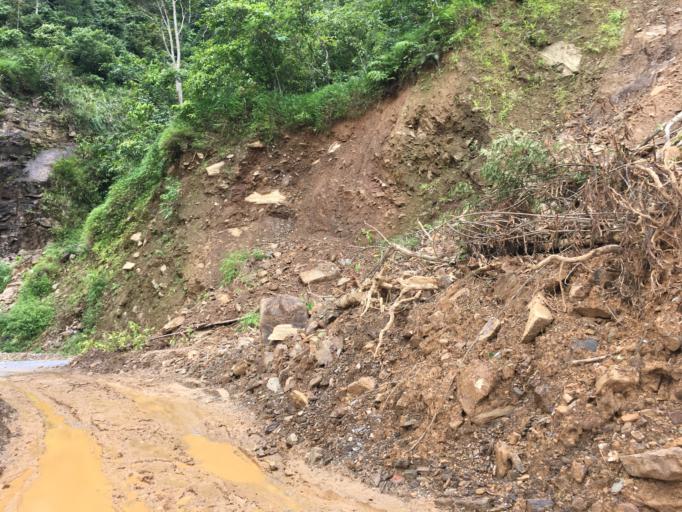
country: VN
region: Ha Giang
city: Thi Tran Tam Son
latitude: 22.9828
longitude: 105.0626
